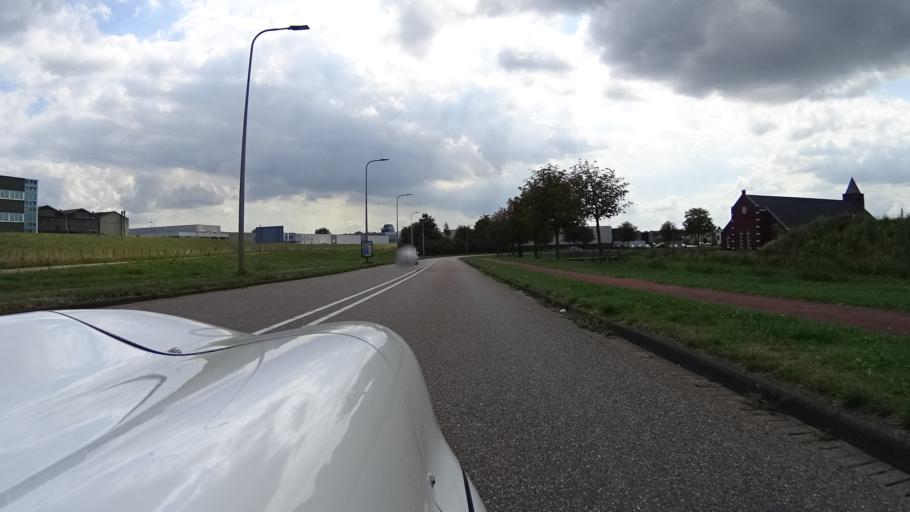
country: NL
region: South Holland
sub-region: Gemeente Ridderkerk
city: Ridderkerk
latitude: 51.8841
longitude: 4.6165
